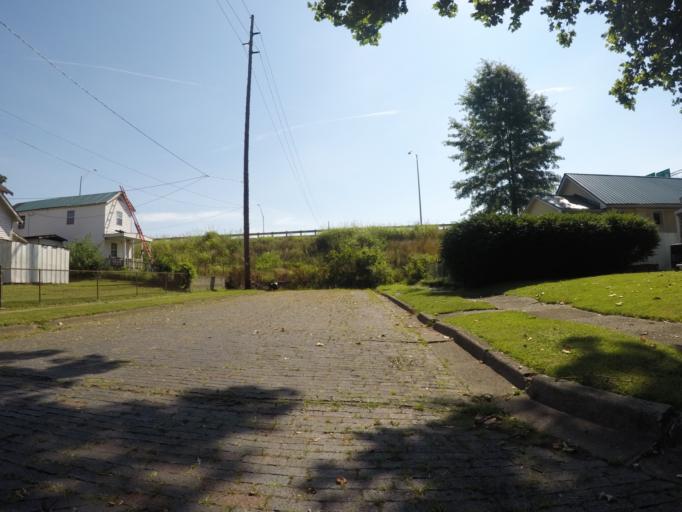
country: US
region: West Virginia
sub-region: Cabell County
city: Huntington
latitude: 38.4060
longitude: -82.4824
